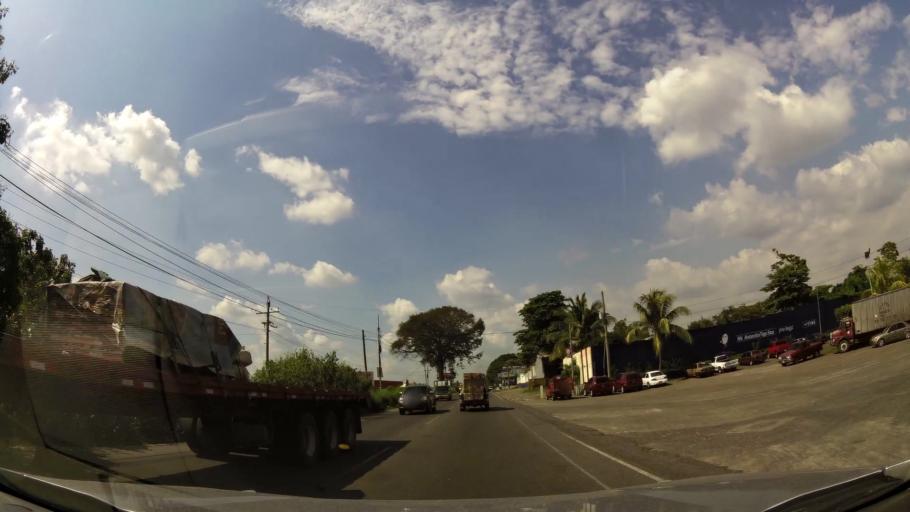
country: GT
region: Suchitepeque
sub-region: Municipio de Cuyotenango
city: Cuyotenango
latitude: 14.5392
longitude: -91.5385
